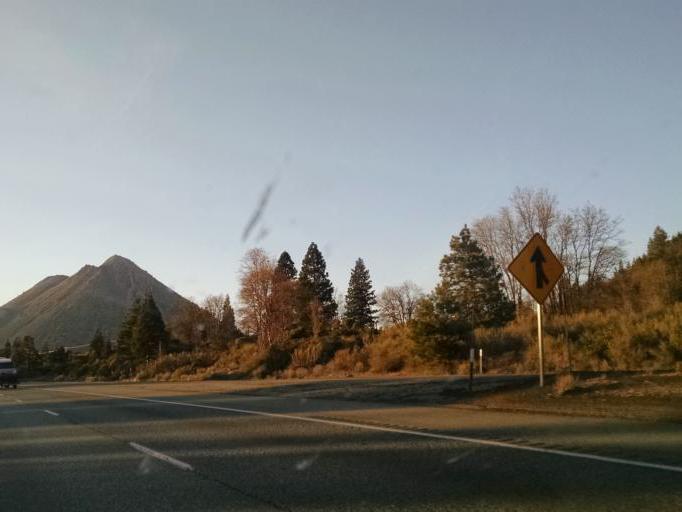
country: US
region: California
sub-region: Siskiyou County
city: Mount Shasta
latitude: 41.3321
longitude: -122.3321
